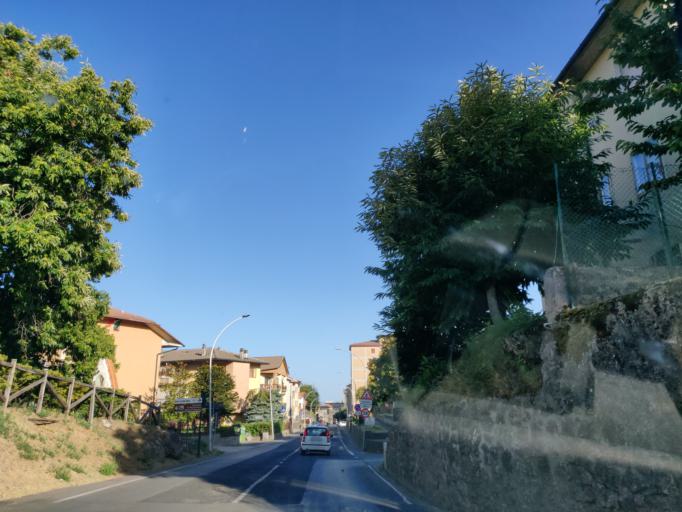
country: IT
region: Tuscany
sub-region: Provincia di Siena
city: Piancastagnaio
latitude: 42.8516
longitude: 11.6886
